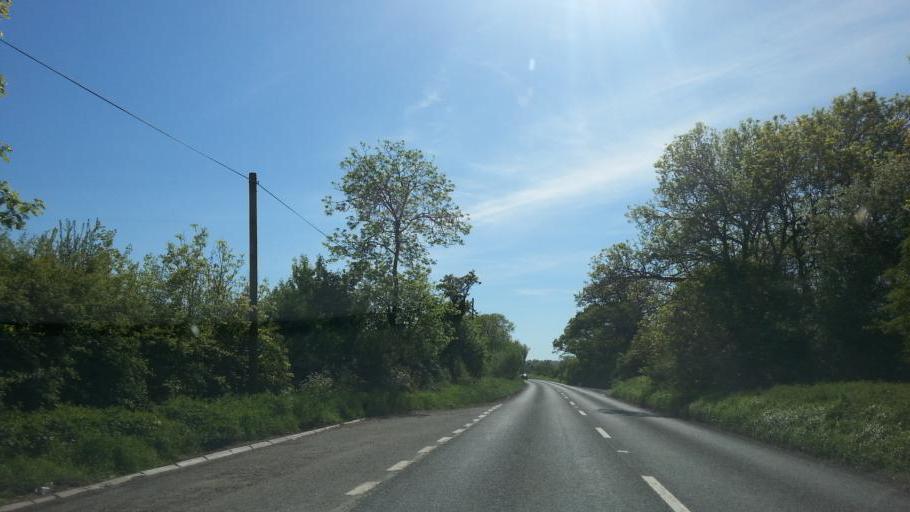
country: GB
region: England
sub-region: Dorset
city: Stalbridge
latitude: 50.9896
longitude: -2.3680
